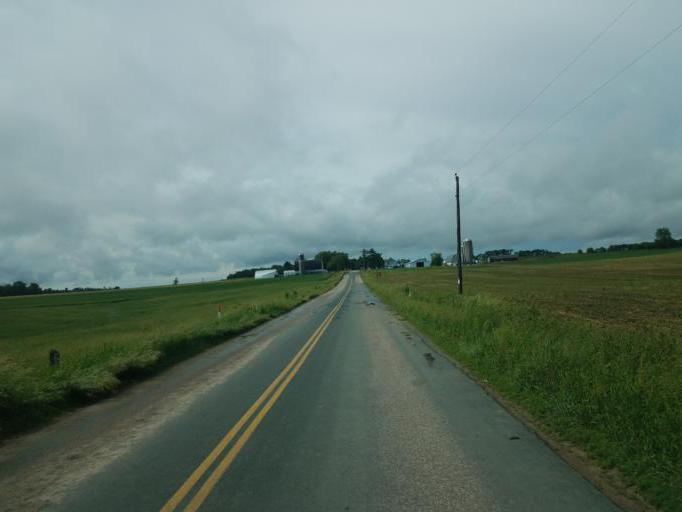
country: US
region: Wisconsin
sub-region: Monroe County
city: Tomah
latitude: 43.8064
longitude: -90.4434
